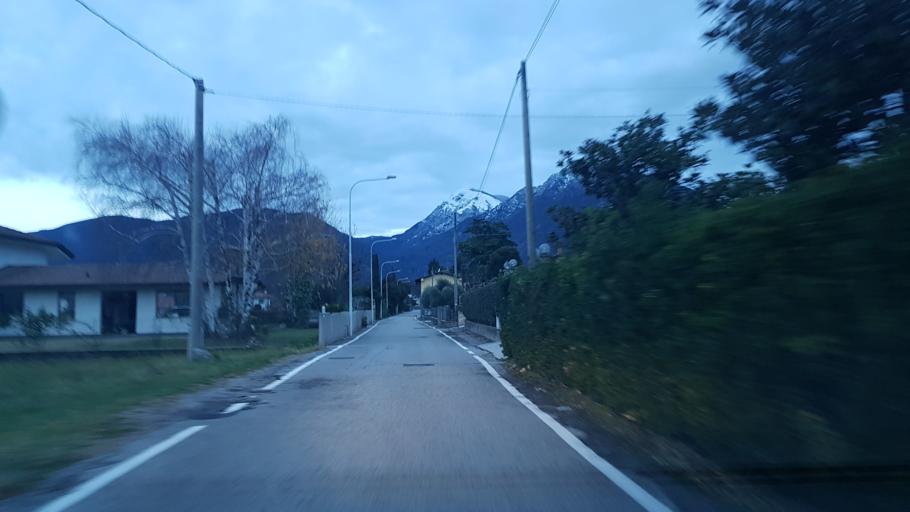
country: IT
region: Friuli Venezia Giulia
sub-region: Provincia di Udine
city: Osoppo
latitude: 46.2545
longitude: 13.0885
